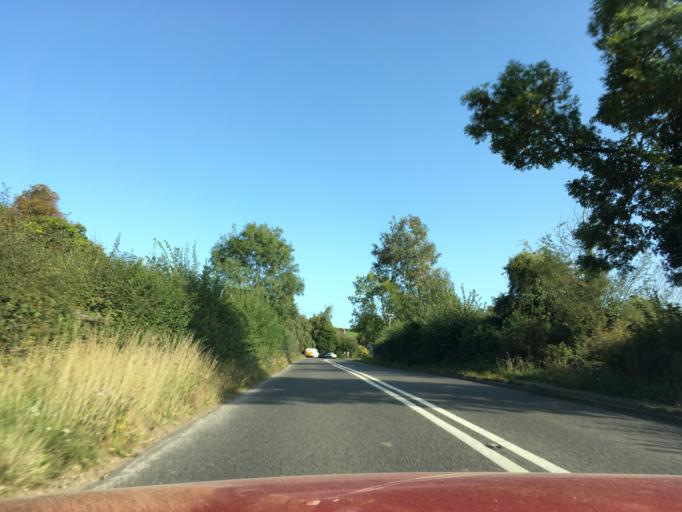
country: GB
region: England
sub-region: Gloucestershire
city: Gloucester
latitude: 51.9070
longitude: -2.2939
